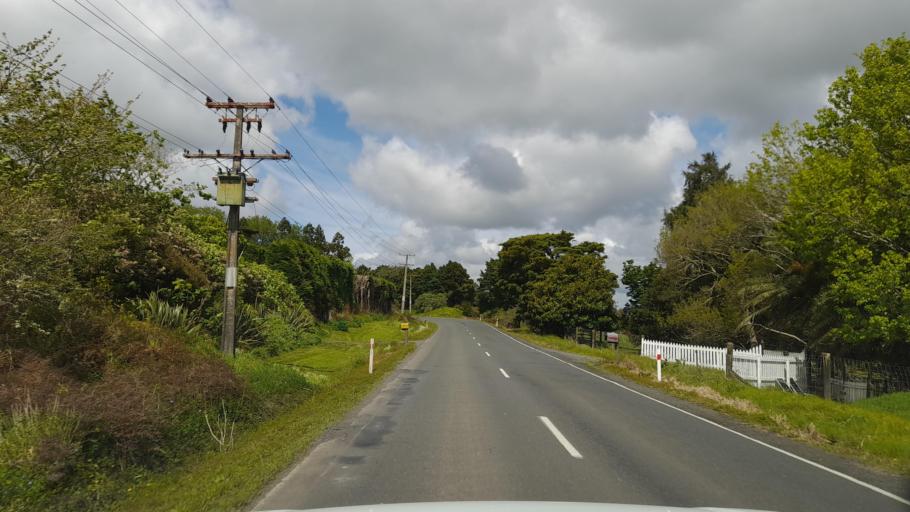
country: NZ
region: Northland
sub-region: Whangarei
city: Maungatapere
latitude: -35.6583
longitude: 174.1647
